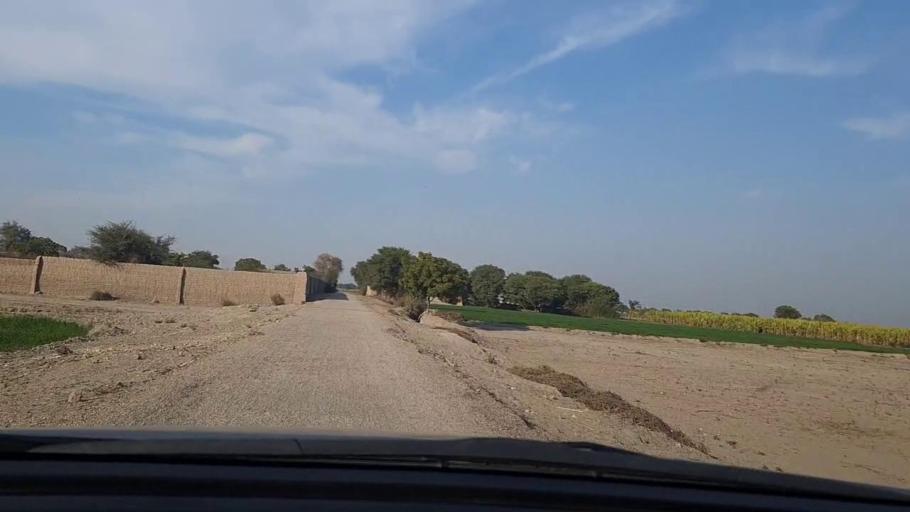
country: PK
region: Sindh
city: Daulatpur
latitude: 26.3219
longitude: 68.0264
